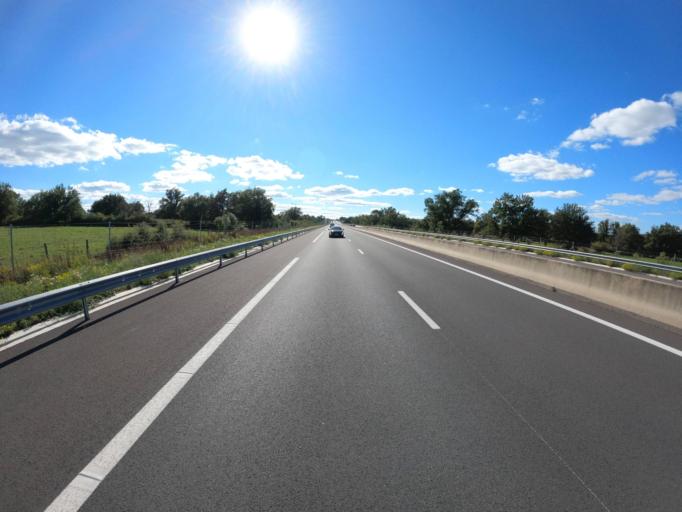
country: FR
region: Auvergne
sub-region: Departement de l'Allier
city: Souvigny
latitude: 46.4472
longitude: 3.2158
